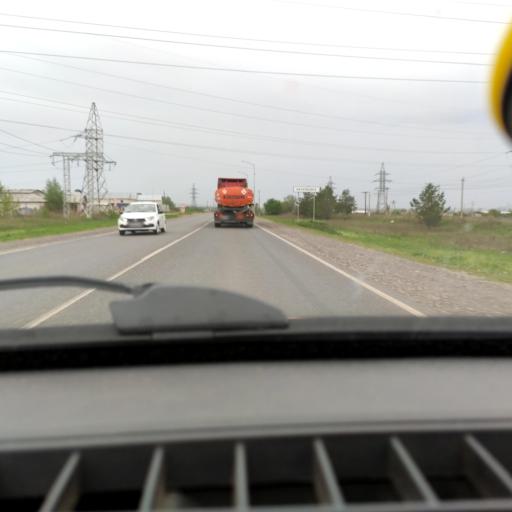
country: RU
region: Samara
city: Zhigulevsk
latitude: 53.5609
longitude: 49.5411
